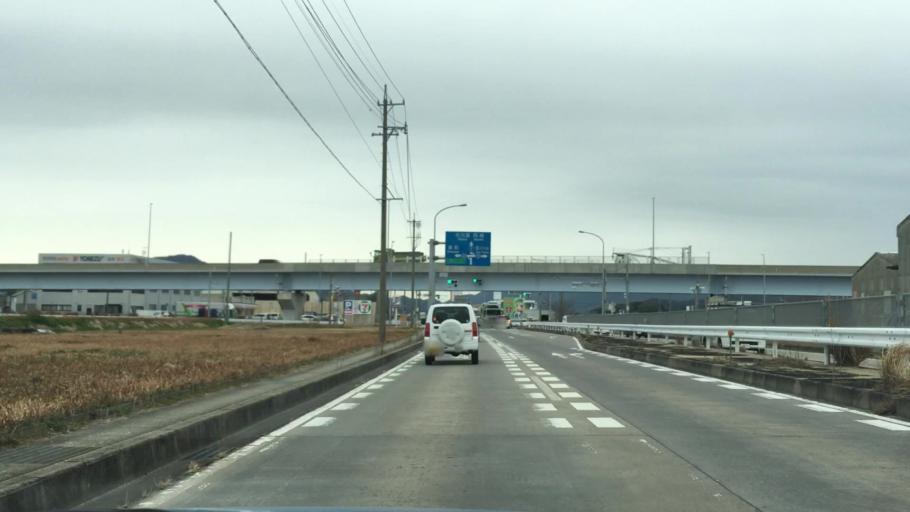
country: JP
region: Aichi
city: Kozakai-cho
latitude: 34.8255
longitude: 137.3409
